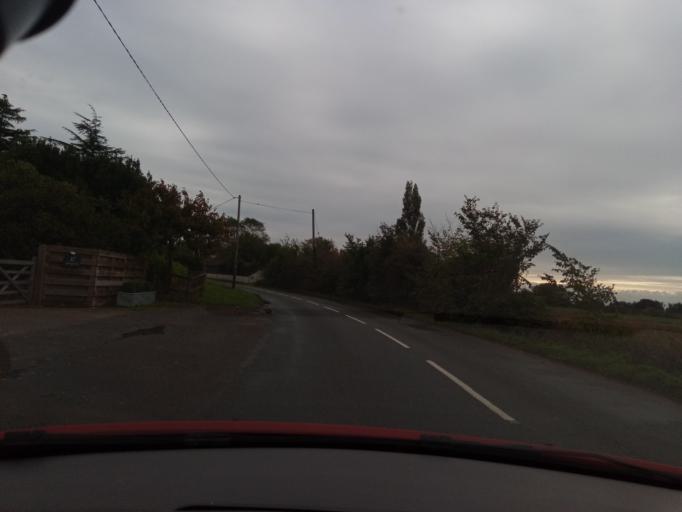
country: GB
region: England
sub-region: Essex
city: West Mersea
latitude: 51.7900
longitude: 0.9356
